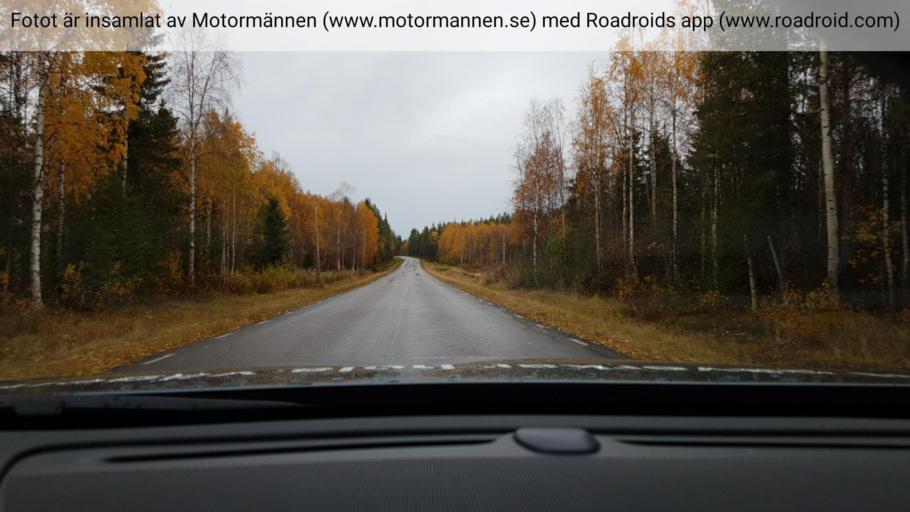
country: SE
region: Norrbotten
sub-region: Pajala Kommun
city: Pajala
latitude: 67.1601
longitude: 22.6566
